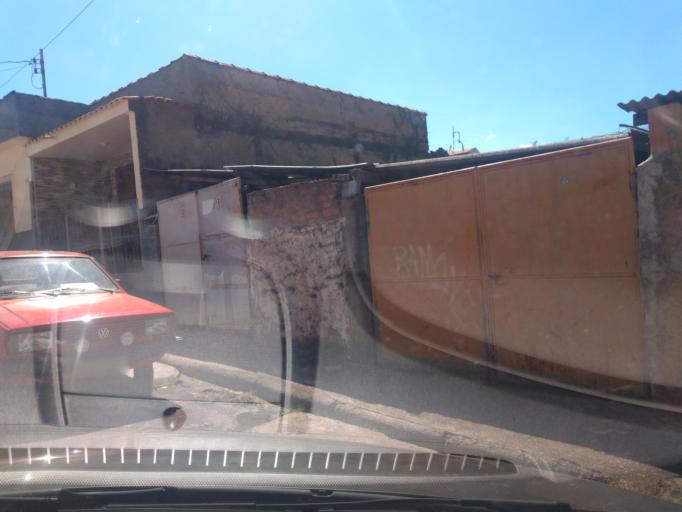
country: BR
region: Minas Gerais
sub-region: Tres Coracoes
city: Tres Coracoes
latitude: -21.6973
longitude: -45.2503
